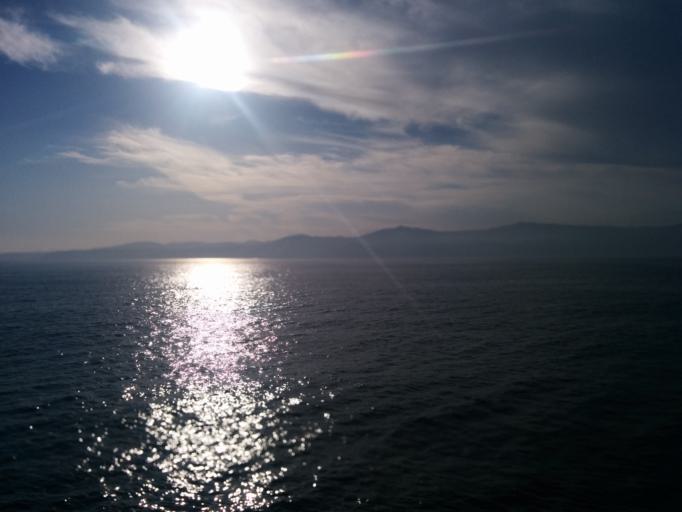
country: MA
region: Tanger-Tetouan
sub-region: Tanger-Assilah
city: Tangier
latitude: 35.8248
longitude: -5.7750
